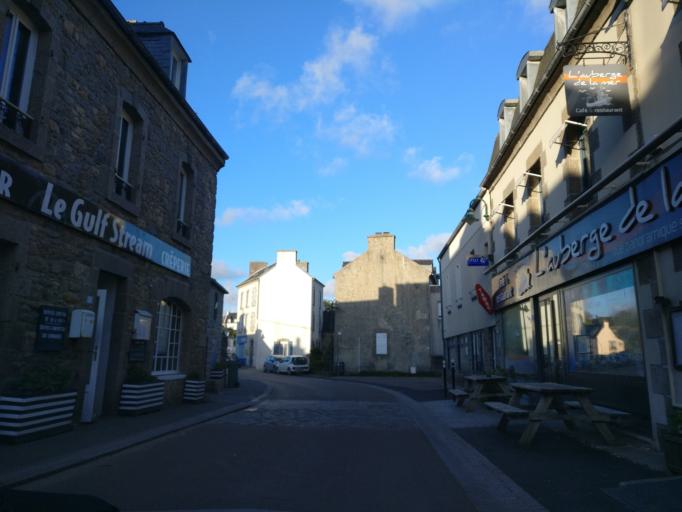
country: FR
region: Brittany
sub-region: Departement du Finistere
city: Lampaul-Plouarzel
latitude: 48.4735
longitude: -4.7523
